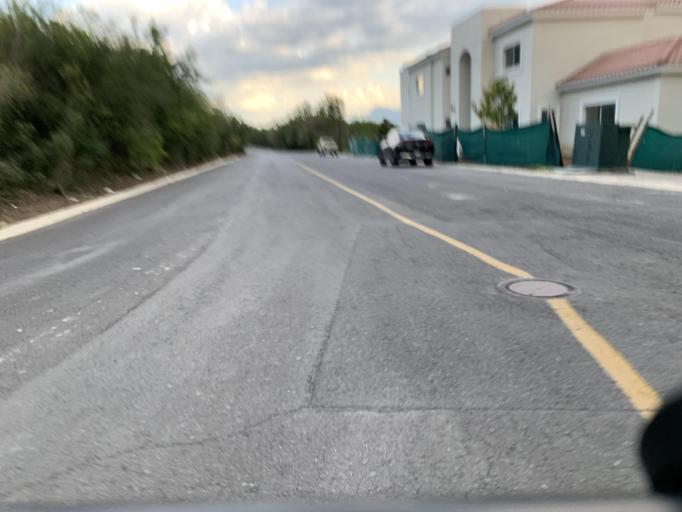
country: MX
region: Nuevo Leon
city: Santiago
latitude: 25.5105
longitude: -100.1810
